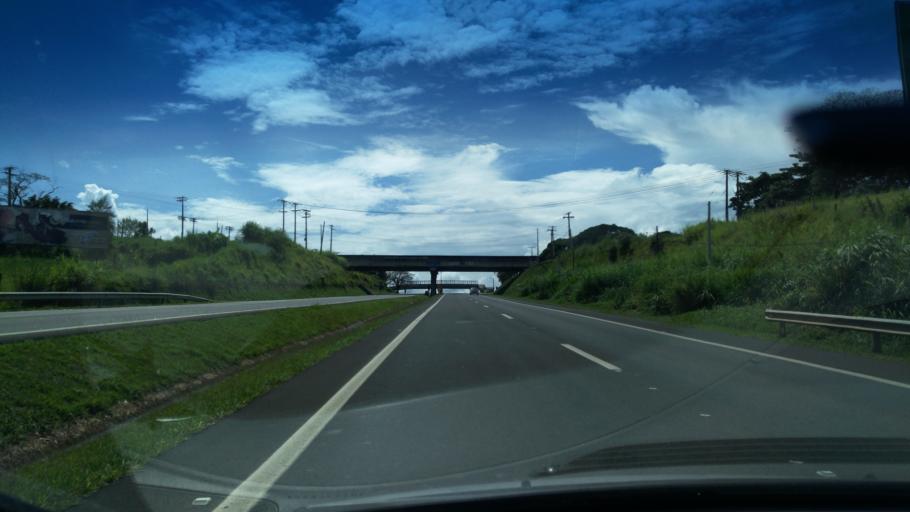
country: BR
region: Sao Paulo
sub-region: Santo Antonio Do Jardim
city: Espirito Santo do Pinhal
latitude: -22.1948
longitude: -46.7732
